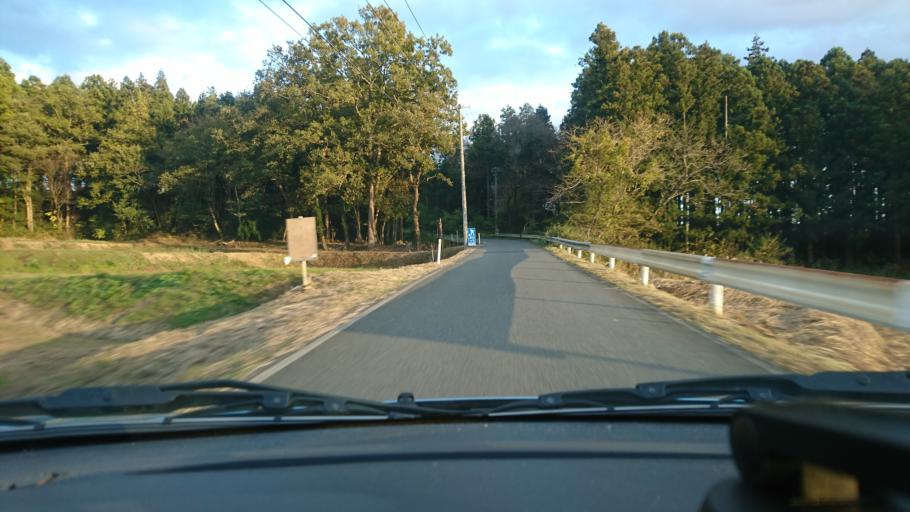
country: JP
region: Iwate
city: Ichinoseki
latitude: 38.7911
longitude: 141.1824
